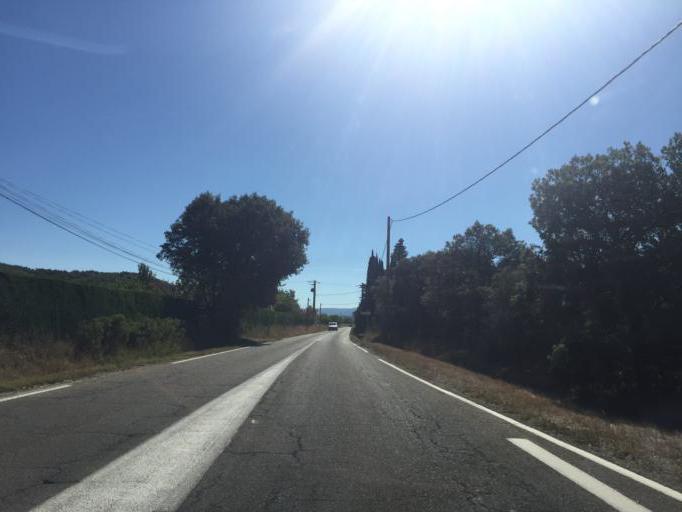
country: FR
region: Provence-Alpes-Cote d'Azur
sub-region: Departement du Vaucluse
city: Saint-Didier
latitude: 44.0286
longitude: 5.0857
